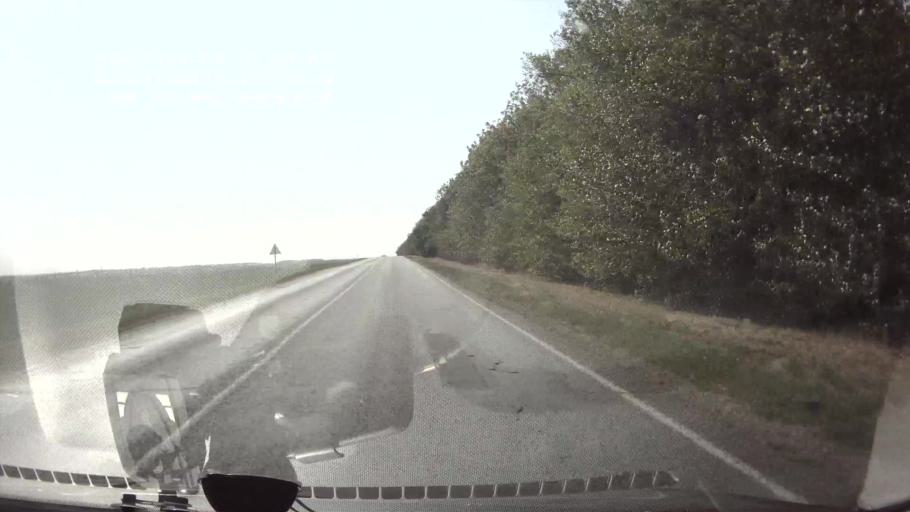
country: RU
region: Krasnodarskiy
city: Dmitriyevskaya
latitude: 45.6711
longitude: 40.7440
